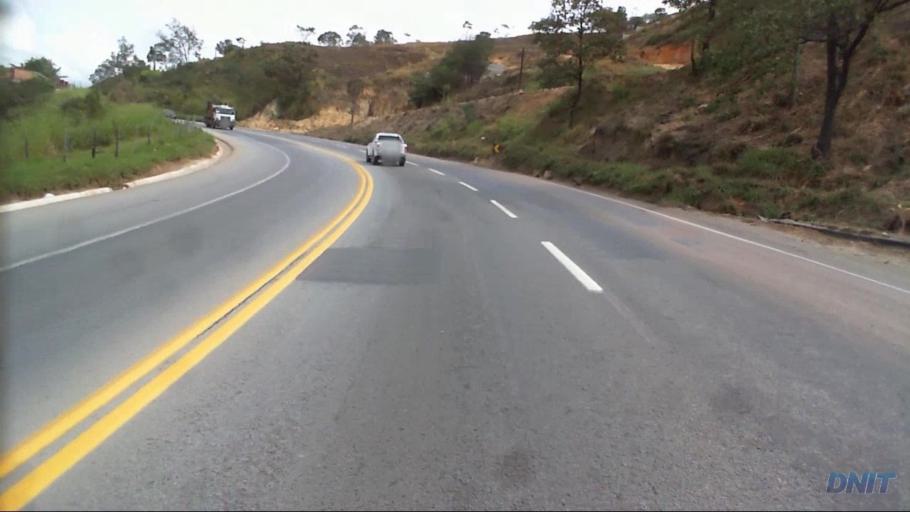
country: BR
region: Minas Gerais
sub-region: Santa Luzia
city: Santa Luzia
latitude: -19.8387
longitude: -43.8850
